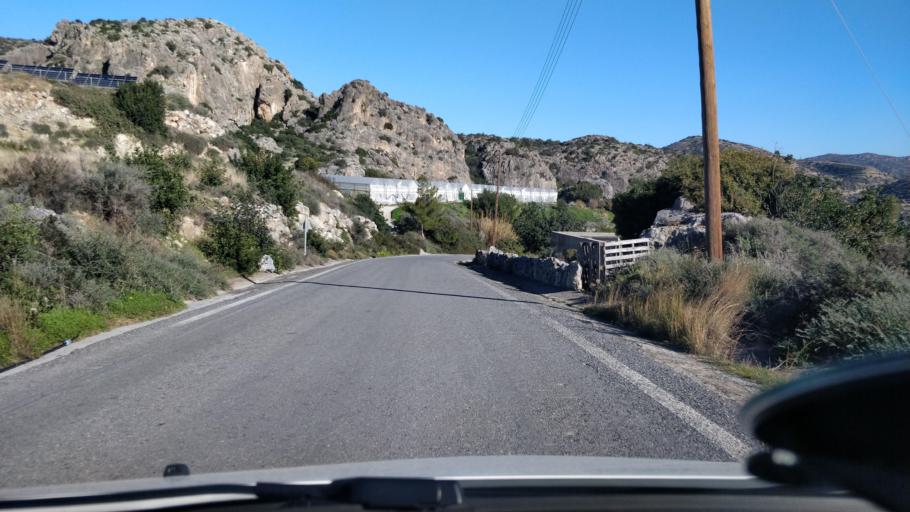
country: GR
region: Crete
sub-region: Nomos Lasithiou
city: Gra Liyia
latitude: 35.0376
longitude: 25.6684
